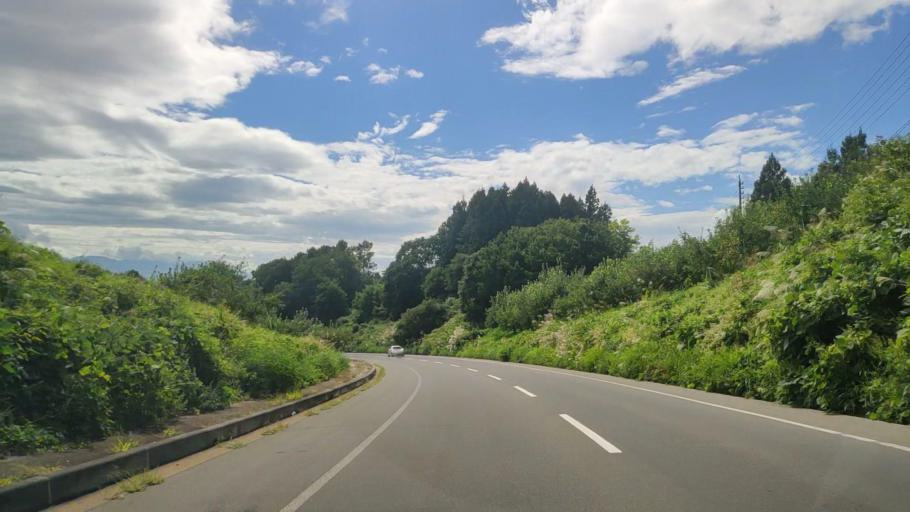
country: JP
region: Nagano
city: Nakano
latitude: 36.7961
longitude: 138.3142
